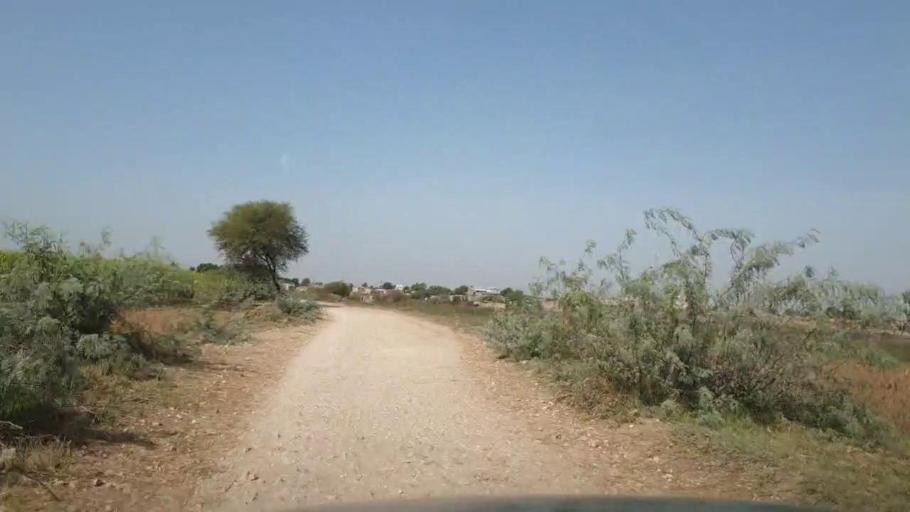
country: PK
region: Sindh
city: Tando Muhammad Khan
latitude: 25.1578
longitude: 68.3912
